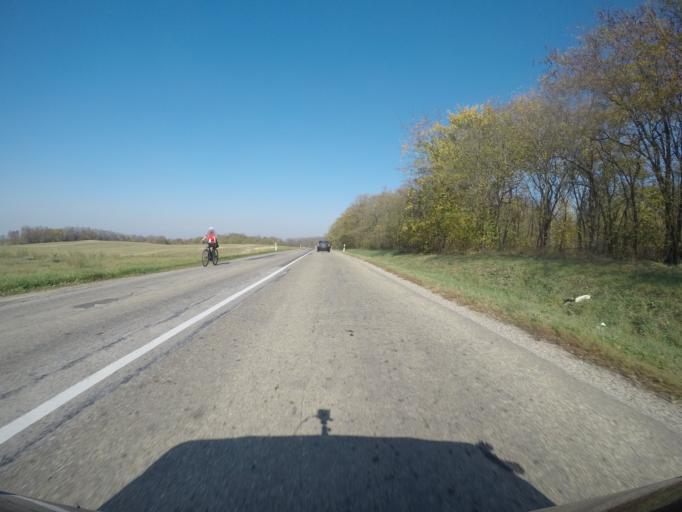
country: HU
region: Tolna
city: Szedres
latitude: 46.4615
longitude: 18.6886
